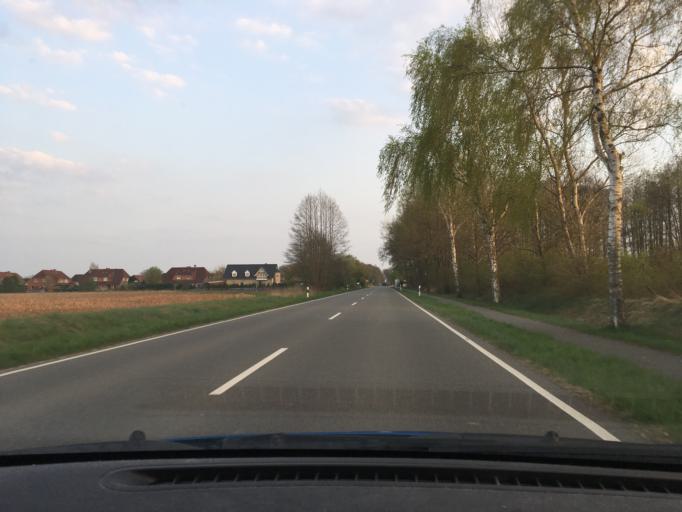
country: DE
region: Lower Saxony
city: Amelinghausen
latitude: 53.1392
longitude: 10.2129
